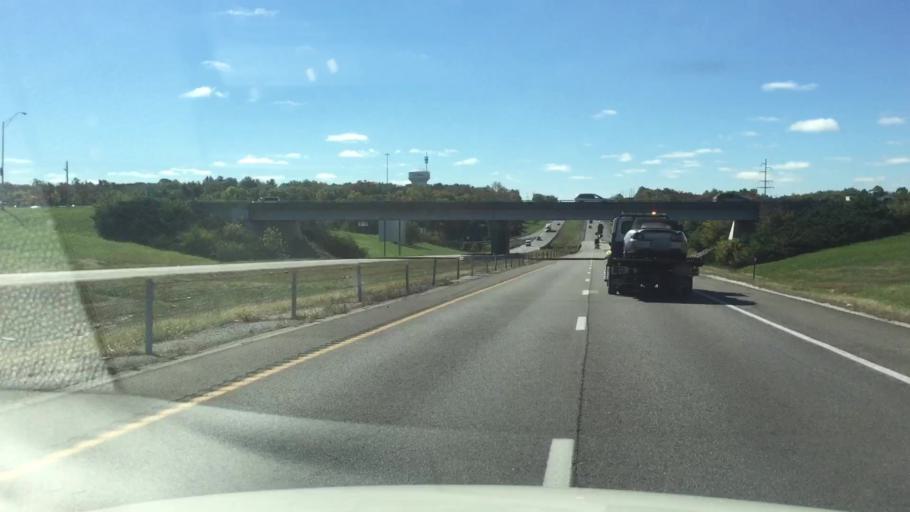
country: US
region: Missouri
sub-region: Boone County
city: Columbia
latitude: 38.9475
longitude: -92.2937
